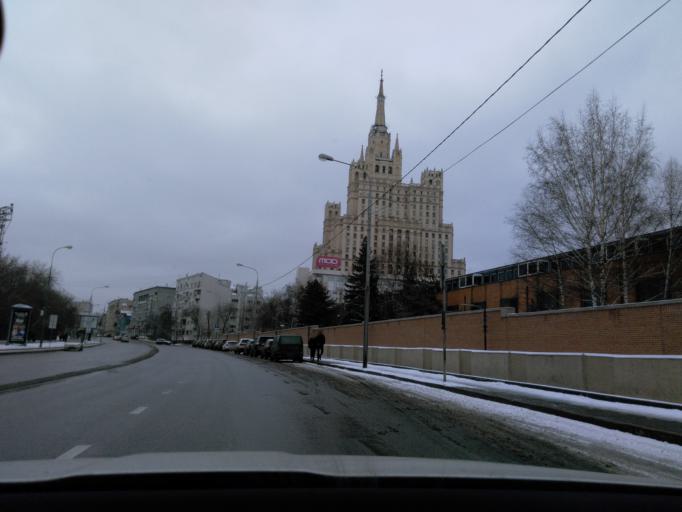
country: RU
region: Moskovskaya
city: Dorogomilovo
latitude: 55.7567
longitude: 37.5781
